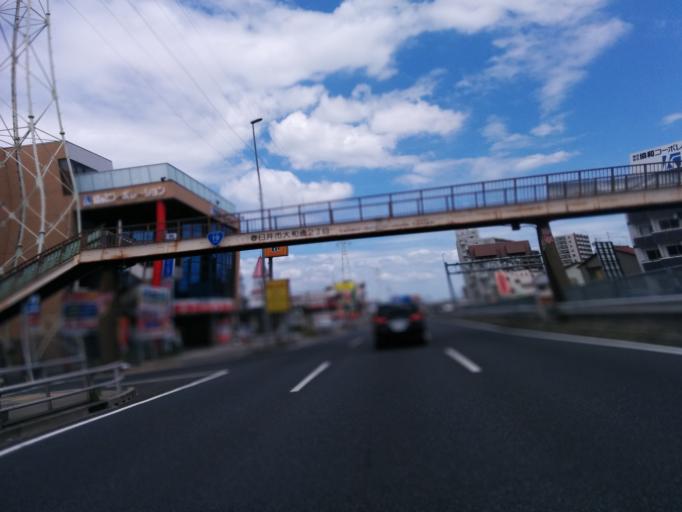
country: JP
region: Aichi
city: Kasugai
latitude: 35.2318
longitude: 136.9509
